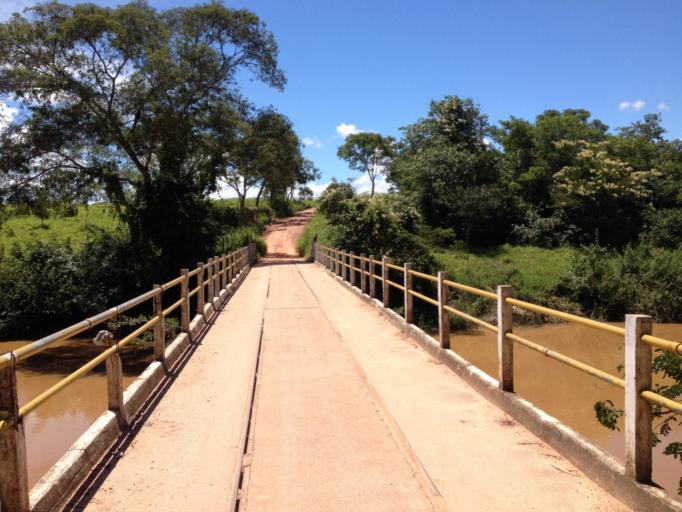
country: BR
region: Goias
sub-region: Ipameri
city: Ipameri
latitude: -17.9731
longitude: -48.1775
